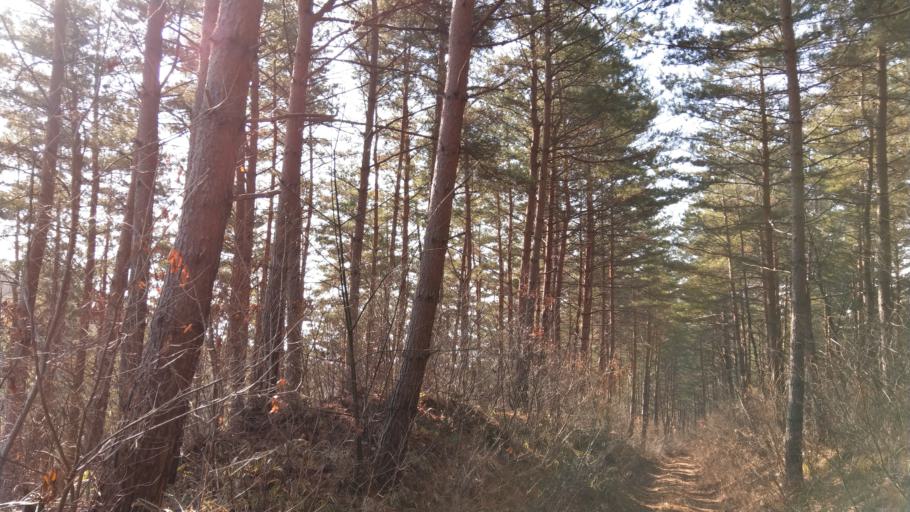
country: JP
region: Nagano
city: Komoro
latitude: 36.3696
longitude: 138.4340
